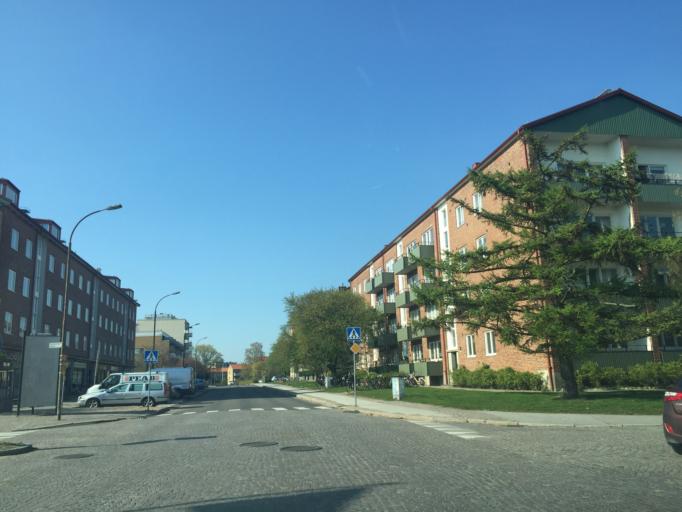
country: SE
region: Skane
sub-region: Lunds Kommun
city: Lund
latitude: 55.7055
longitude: 13.1836
